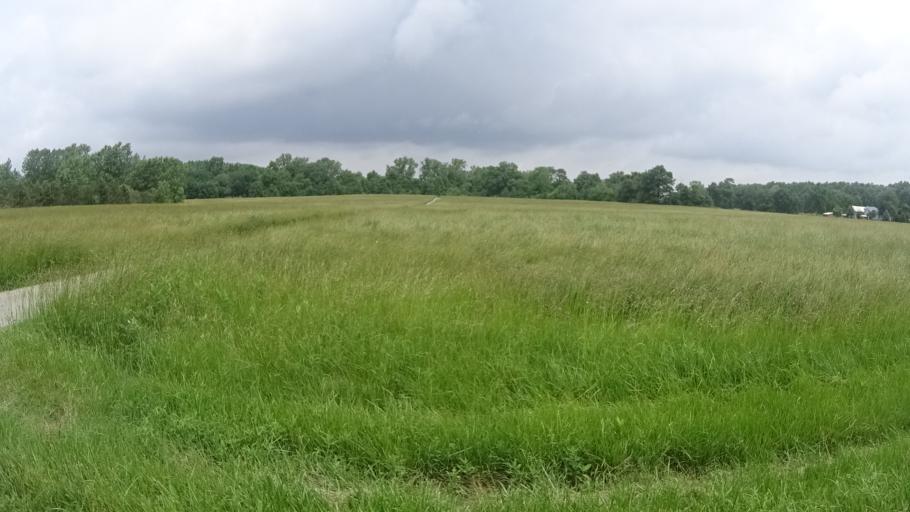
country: US
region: Ohio
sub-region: Huron County
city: Bellevue
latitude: 41.3261
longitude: -82.8234
